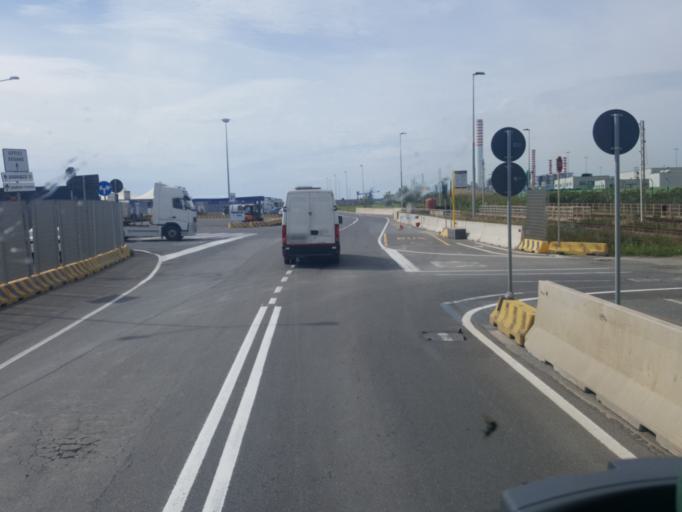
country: IT
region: Latium
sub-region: Citta metropolitana di Roma Capitale
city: Civitavecchia
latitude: 42.1092
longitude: 11.7739
